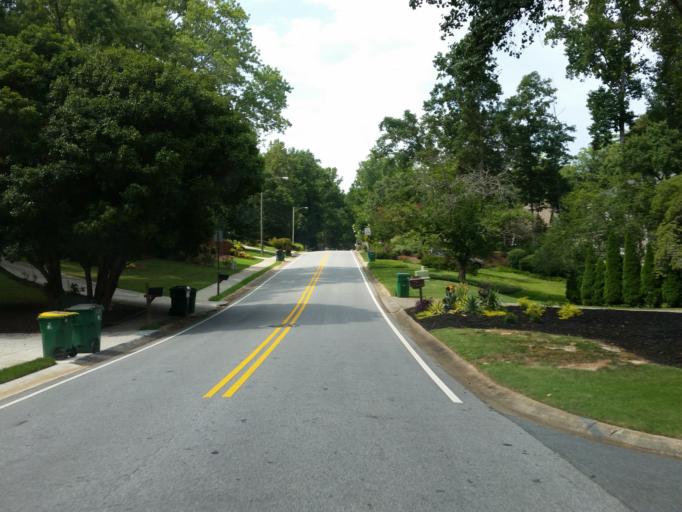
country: US
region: Georgia
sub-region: Fulton County
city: Sandy Springs
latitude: 33.9685
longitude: -84.4462
